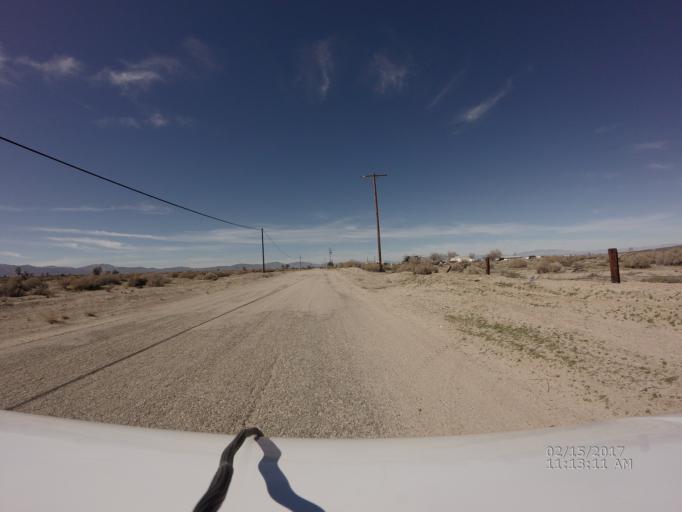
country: US
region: California
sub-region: Los Angeles County
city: Lake Los Angeles
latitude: 34.5874
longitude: -117.8935
